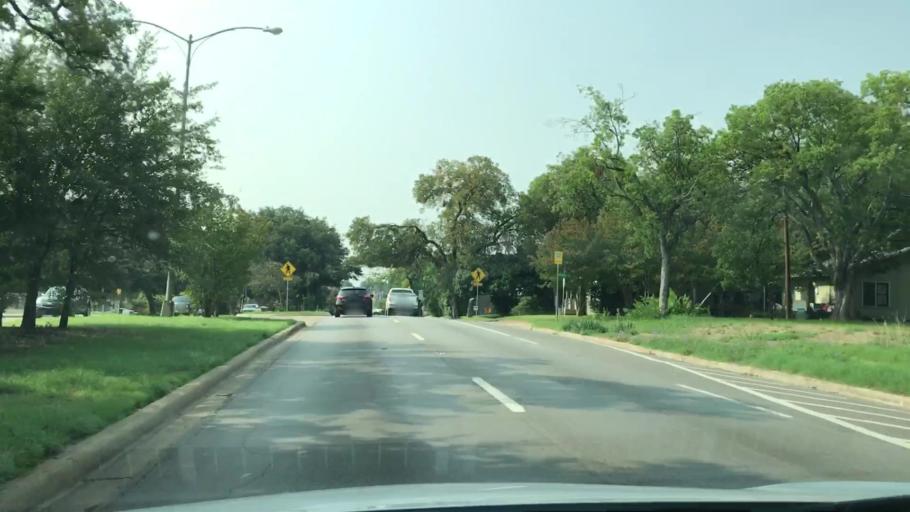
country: US
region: Texas
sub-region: Dallas County
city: Dallas
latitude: 32.7536
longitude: -96.8375
